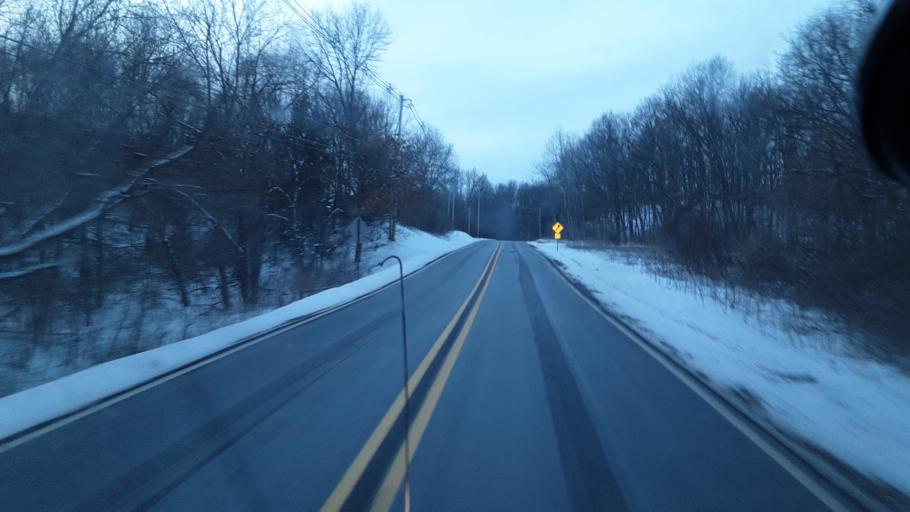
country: US
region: Michigan
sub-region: Jackson County
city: Grass Lake
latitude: 42.3026
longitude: -84.2058
